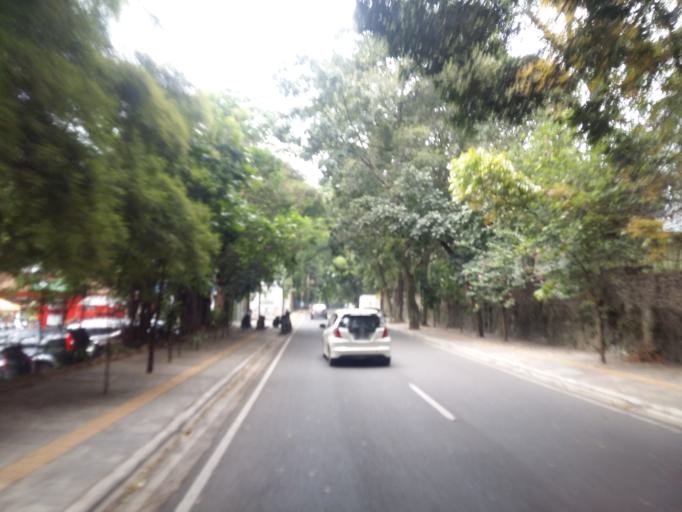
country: ID
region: West Java
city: Bandung
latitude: -6.8894
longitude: 107.6079
